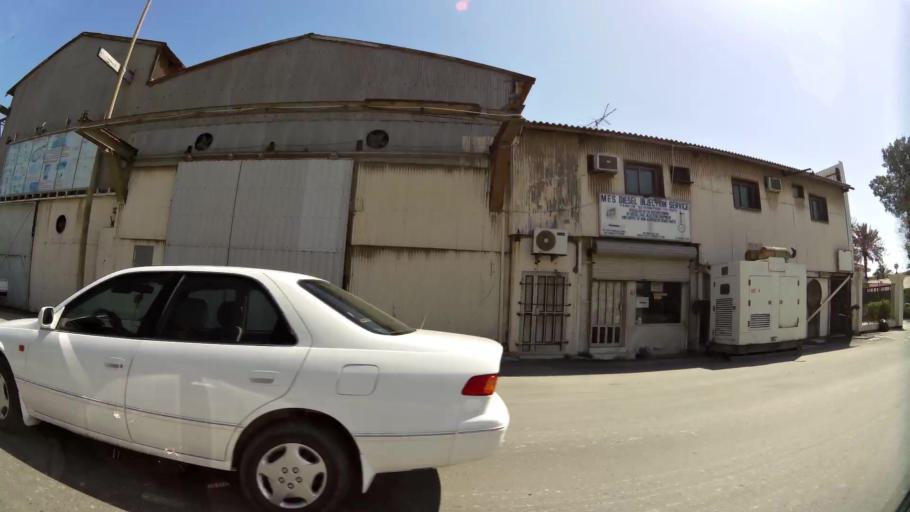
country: BH
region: Manama
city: Manama
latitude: 26.1990
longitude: 50.5988
